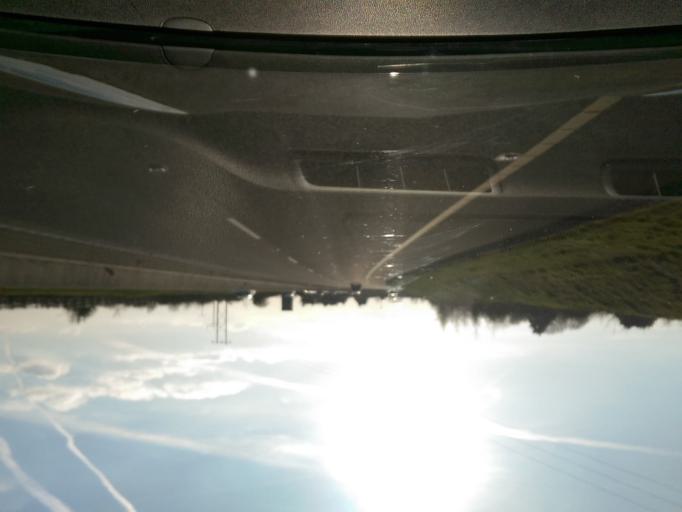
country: IE
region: Leinster
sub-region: Laois
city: Mountrath
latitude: 52.9949
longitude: -7.4173
